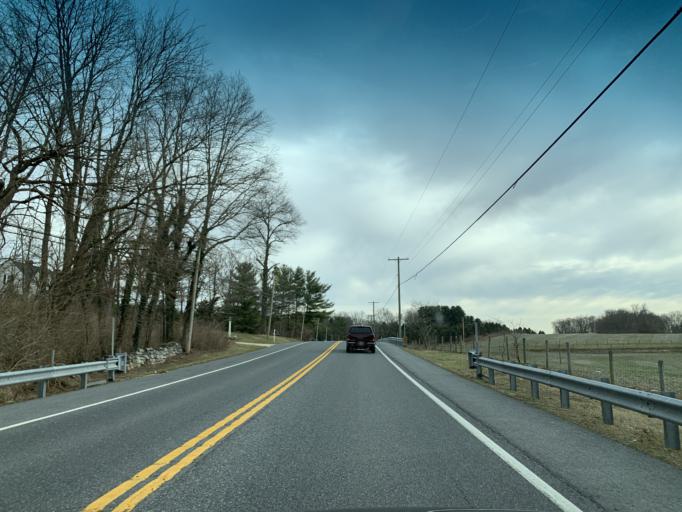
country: US
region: Maryland
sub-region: Washington County
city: Robinwood
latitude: 39.5844
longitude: -77.6955
